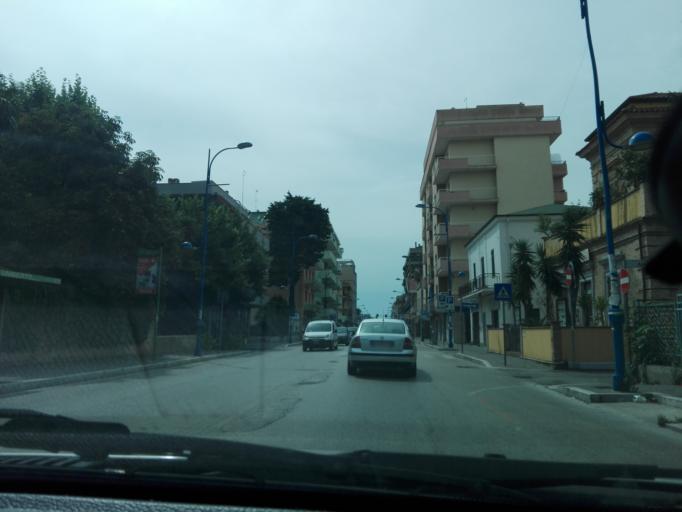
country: IT
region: Abruzzo
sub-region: Provincia di Pescara
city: Montesilvano Marina
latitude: 42.5138
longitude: 14.1529
